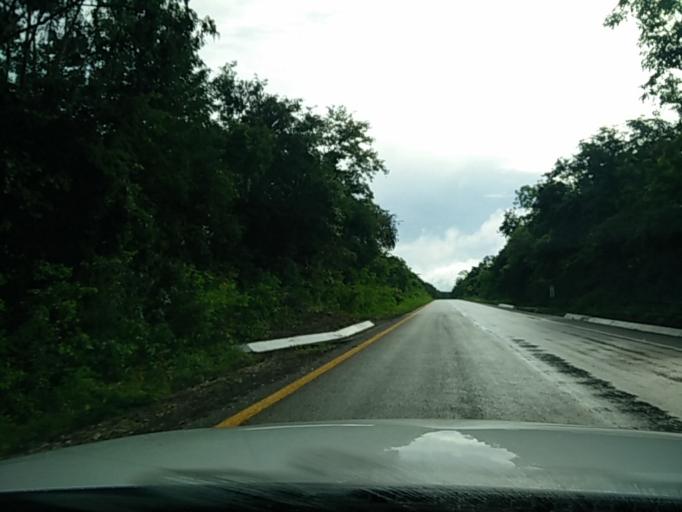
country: MX
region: Yucatan
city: Tunkas
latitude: 20.7658
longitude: -88.8040
